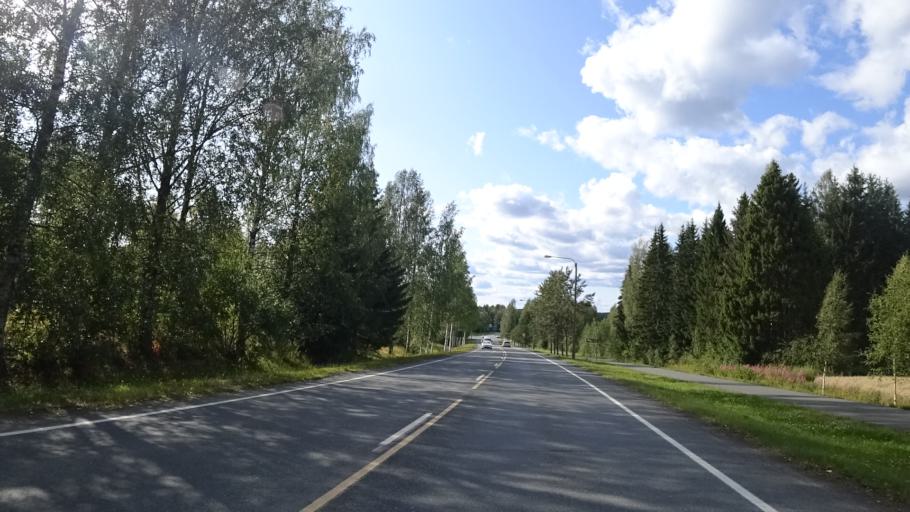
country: FI
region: North Karelia
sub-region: Keski-Karjala
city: Tohmajaervi
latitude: 62.2282
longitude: 30.3268
